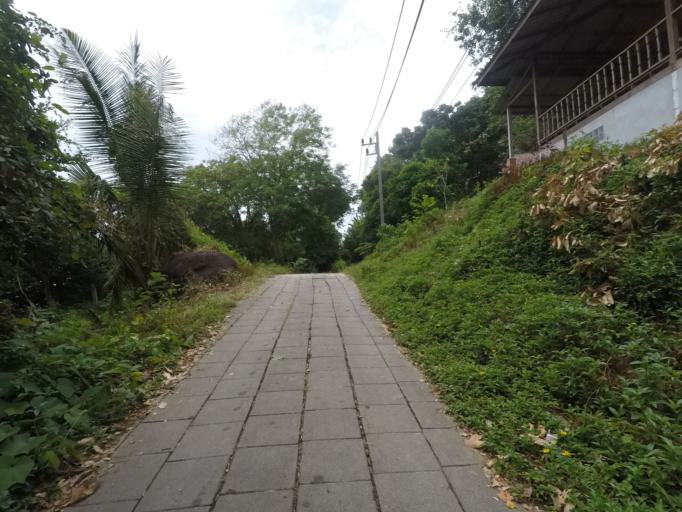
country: TH
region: Phangnga
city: Ban Phru Nai
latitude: 7.7698
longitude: 98.7683
